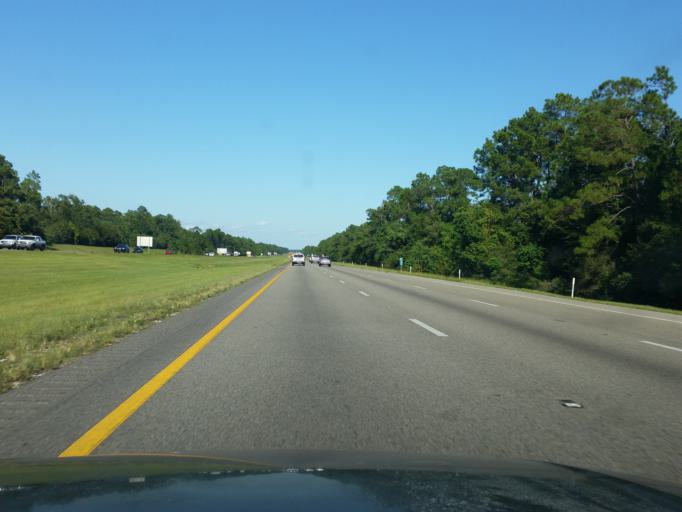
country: US
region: Mississippi
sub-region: Hancock County
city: Diamondhead
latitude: 30.3740
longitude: -89.3720
